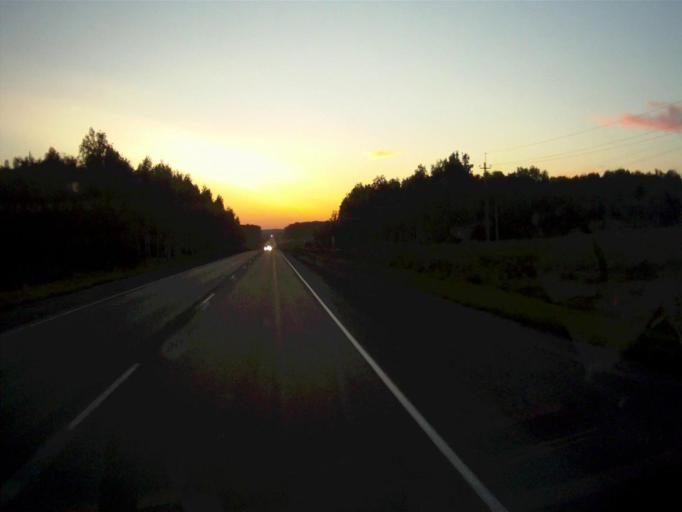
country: RU
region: Chelyabinsk
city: Poletayevo
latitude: 55.2179
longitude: 61.0394
